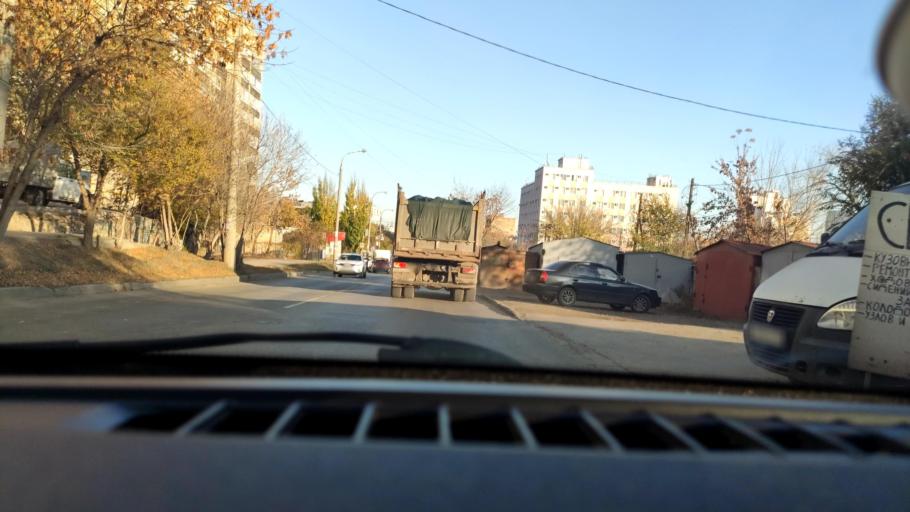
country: RU
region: Samara
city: Samara
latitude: 53.1873
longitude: 50.1890
